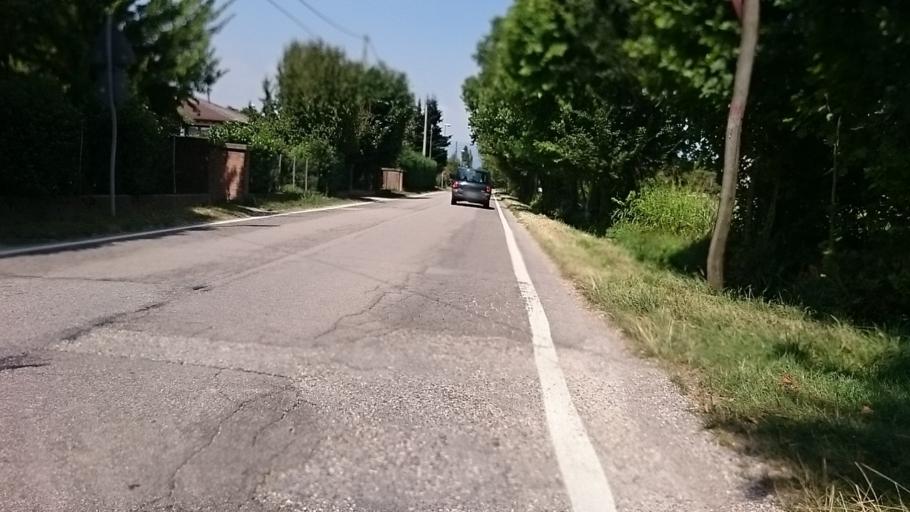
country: IT
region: Veneto
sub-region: Provincia di Vicenza
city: Rosa
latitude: 45.6871
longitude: 11.7399
